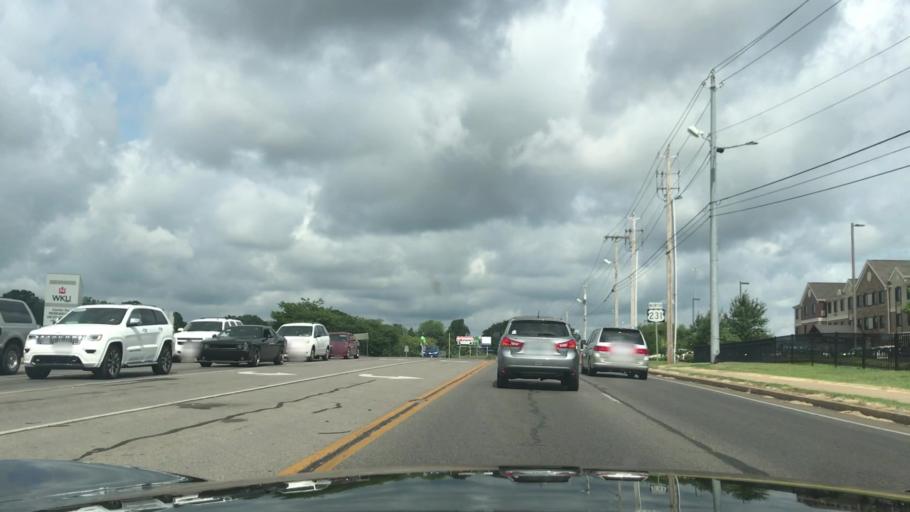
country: US
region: Kentucky
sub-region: Warren County
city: Bowling Green
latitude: 36.9625
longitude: -86.4683
